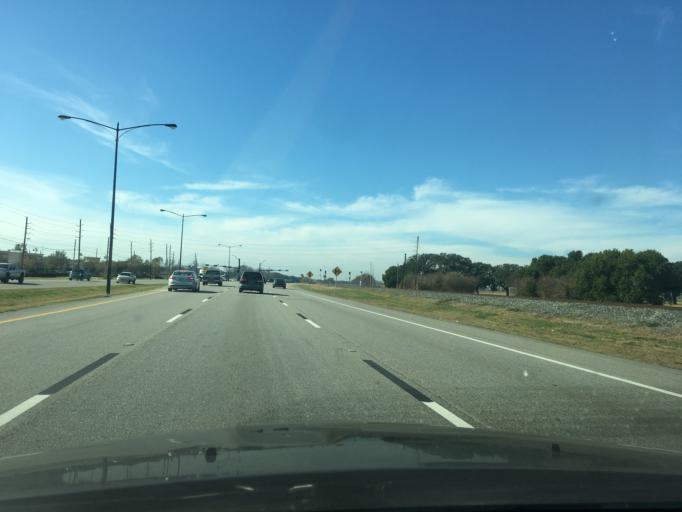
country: US
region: Texas
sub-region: Fort Bend County
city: Sugar Land
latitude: 29.6096
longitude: -95.6579
